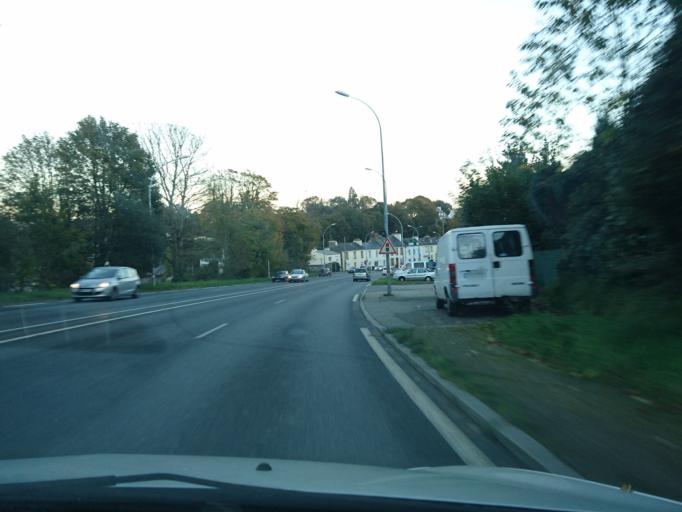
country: FR
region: Brittany
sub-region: Departement du Finistere
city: Bohars
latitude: 48.4115
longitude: -4.5291
